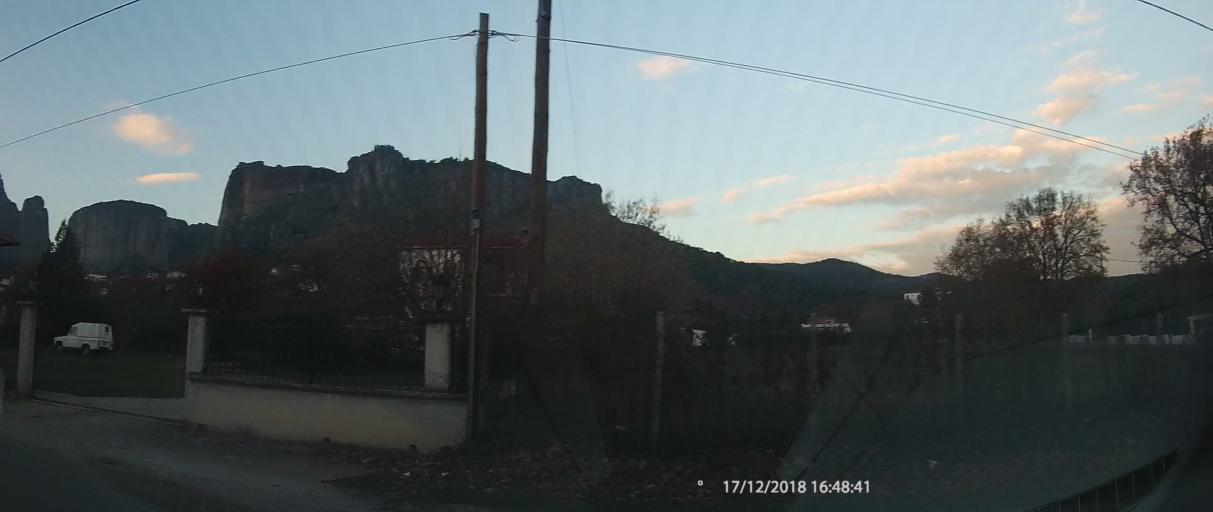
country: GR
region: Thessaly
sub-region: Trikala
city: Kalampaka
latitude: 39.7007
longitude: 21.6404
